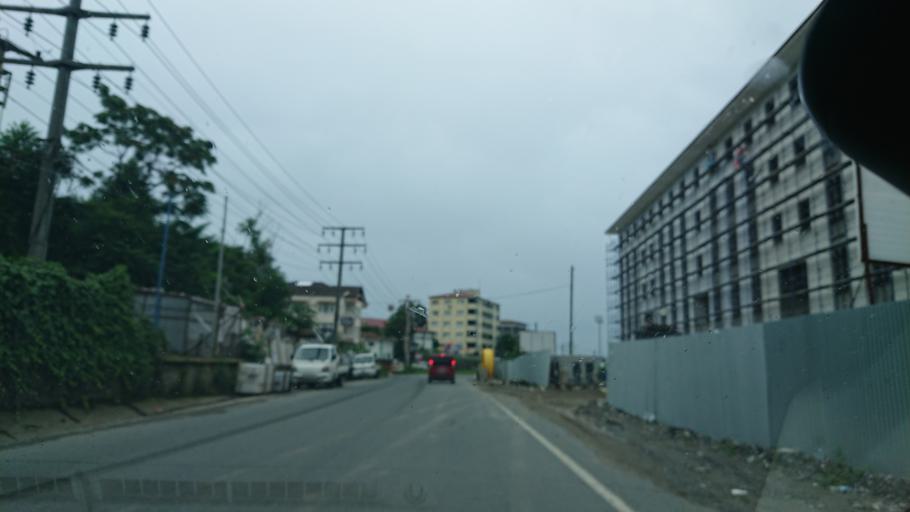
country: TR
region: Rize
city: Gundogdu
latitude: 41.0389
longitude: 40.5772
